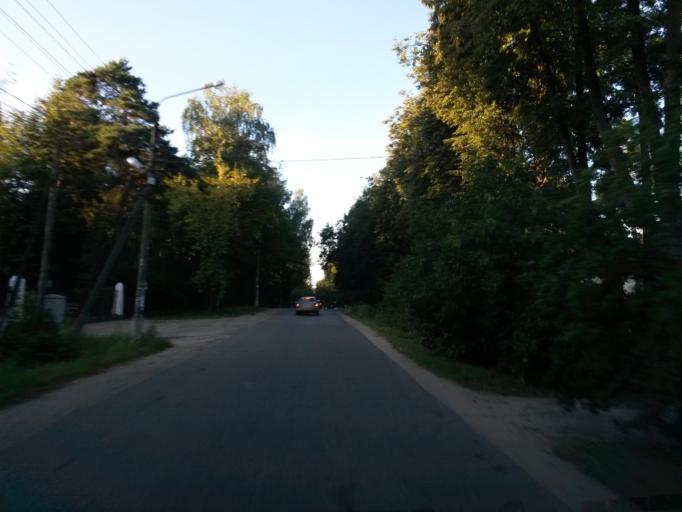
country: RU
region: Moskovskaya
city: Mamontovka
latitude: 55.9773
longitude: 37.8369
